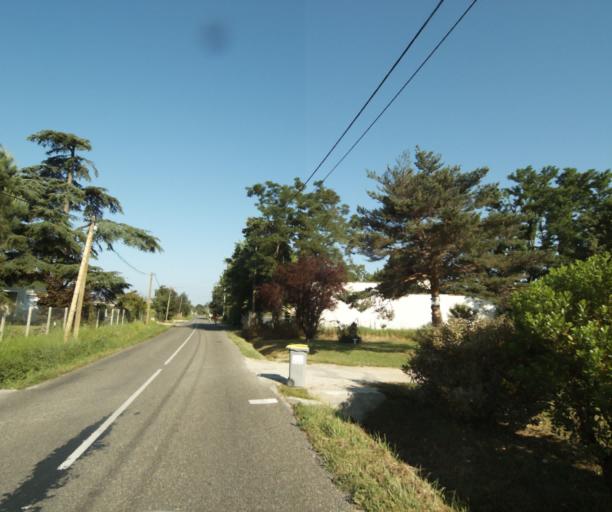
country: FR
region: Midi-Pyrenees
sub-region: Departement du Tarn-et-Garonne
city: Saint-Nauphary
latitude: 44.0150
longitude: 1.4275
